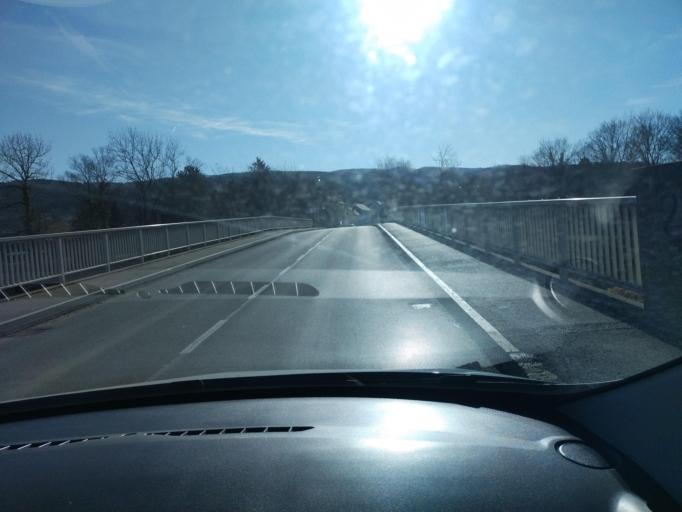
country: AT
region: Lower Austria
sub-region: Politischer Bezirk Wiener Neustadt
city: Lanzenkirchen
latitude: 47.7487
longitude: 16.2510
